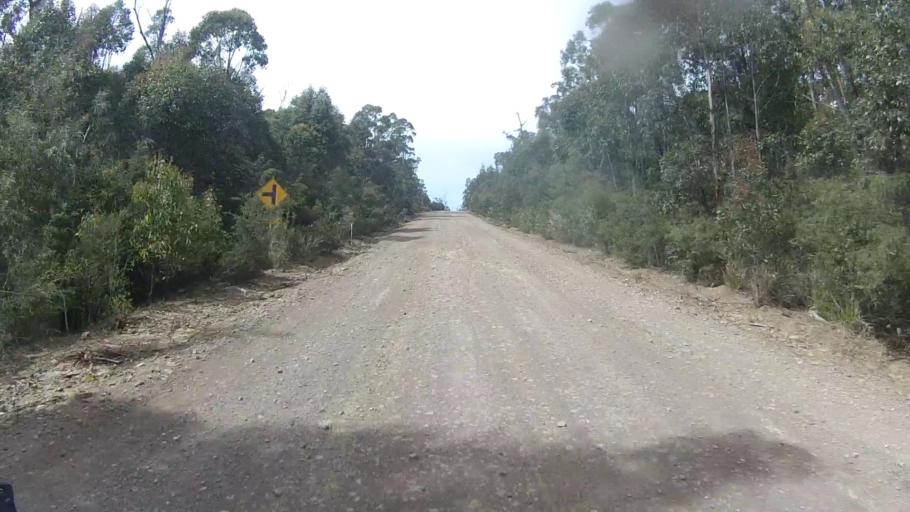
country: AU
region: Tasmania
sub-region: Sorell
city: Sorell
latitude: -42.7561
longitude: 147.8296
